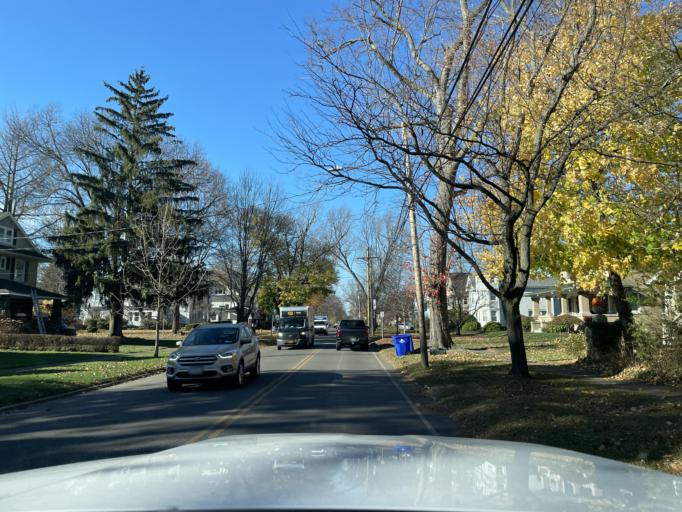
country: US
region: New York
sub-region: Orleans County
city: Medina
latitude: 43.2206
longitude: -78.3999
